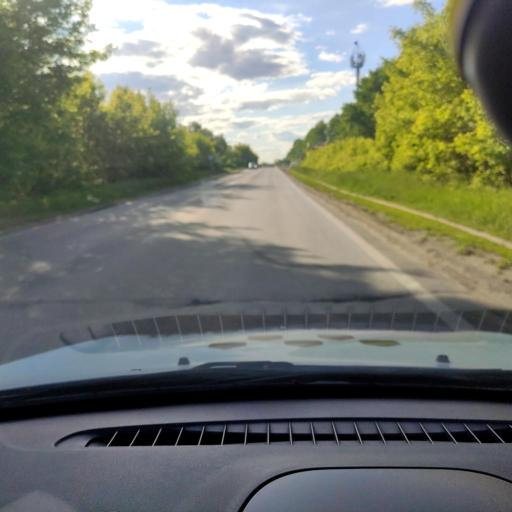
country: RU
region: Samara
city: Podstepki
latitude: 53.5779
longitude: 49.0711
